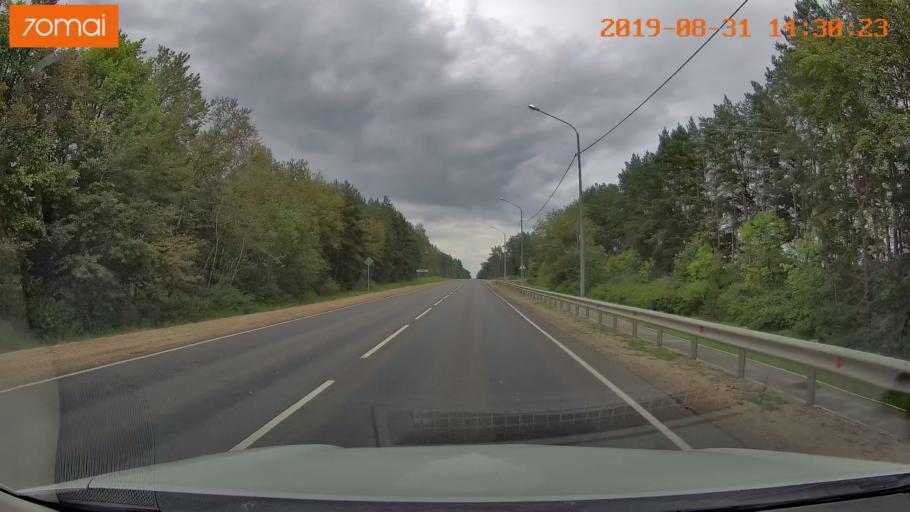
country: RU
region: Smolensk
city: Yekimovichi
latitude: 54.1312
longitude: 33.3497
